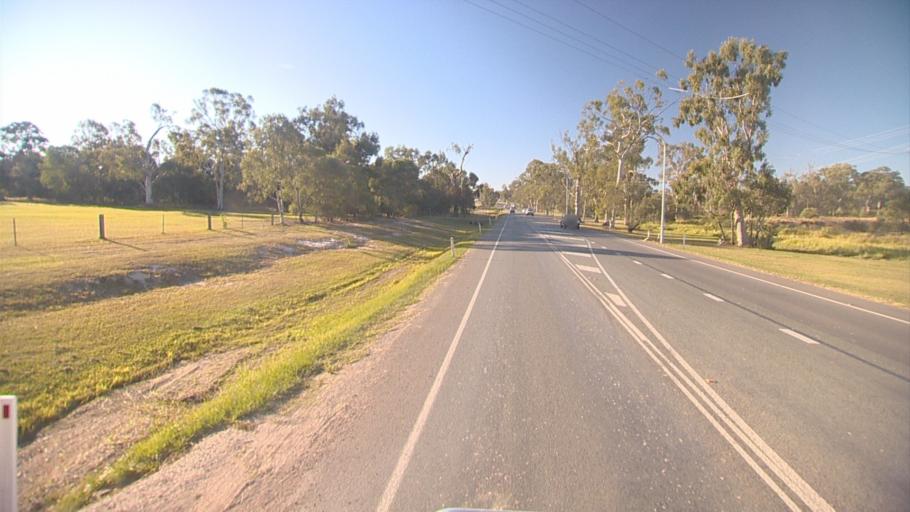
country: AU
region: Queensland
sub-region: Logan
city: Logan Reserve
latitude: -27.7171
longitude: 153.0920
